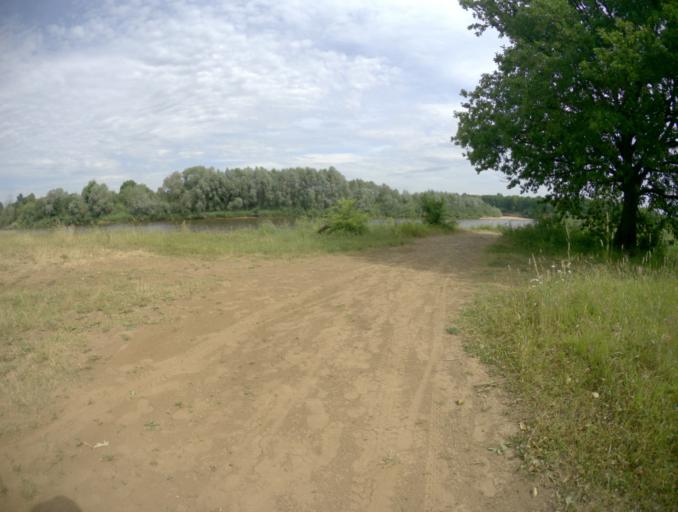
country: RU
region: Vladimir
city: Raduzhnyy
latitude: 56.0329
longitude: 40.2744
